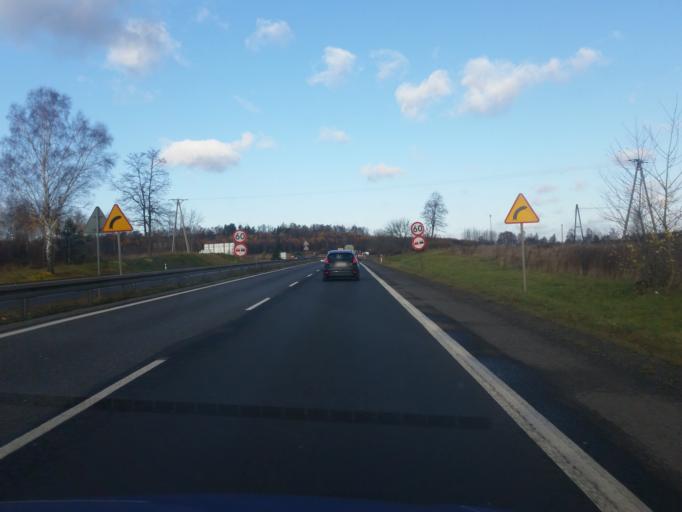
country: PL
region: Silesian Voivodeship
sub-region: Powiat myszkowski
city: Kozieglowy
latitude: 50.6305
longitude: 19.1389
